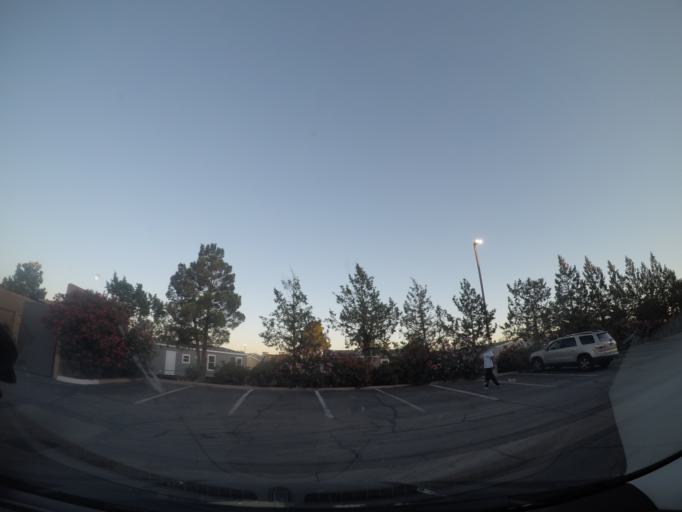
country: US
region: New Mexico
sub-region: Dona Ana County
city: Las Cruces
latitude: 32.2920
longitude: -106.7863
